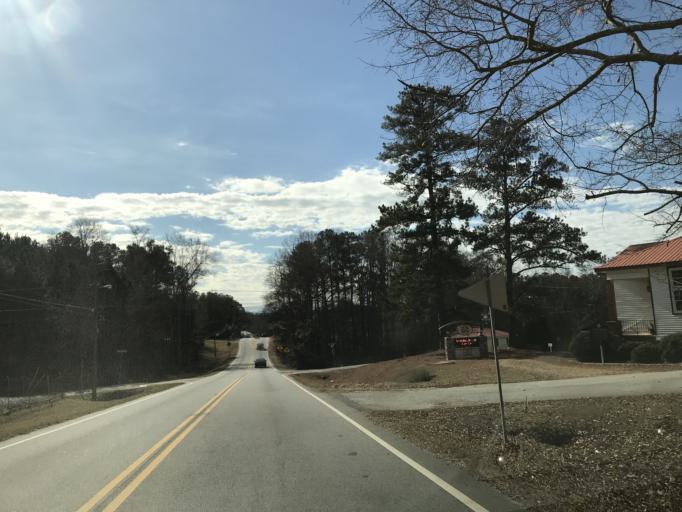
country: US
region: Georgia
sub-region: Paulding County
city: Hiram
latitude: 33.8816
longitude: -84.7595
